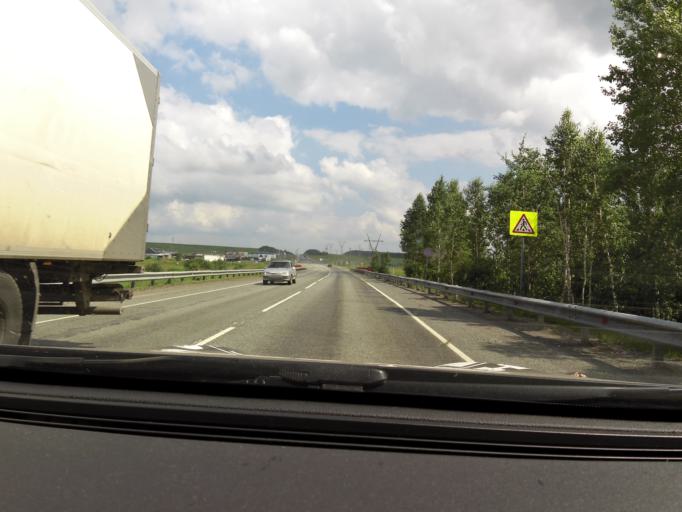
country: RU
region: Sverdlovsk
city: Achit
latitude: 56.7832
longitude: 57.9005
